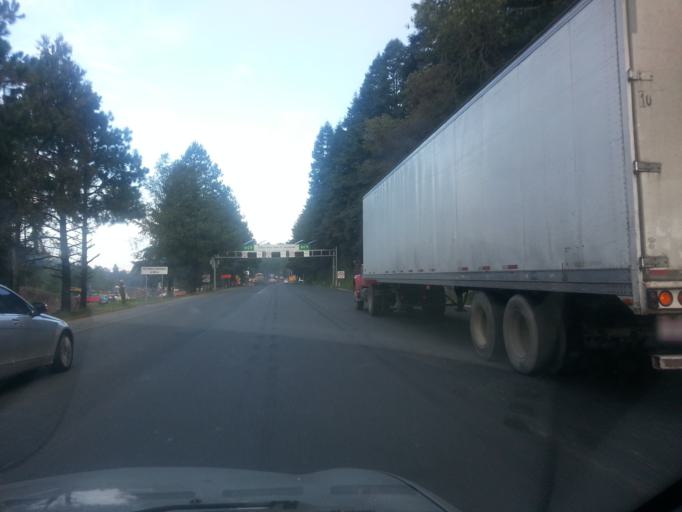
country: MX
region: Morelos
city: San Jeronimo Acazulco
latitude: 19.2989
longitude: -99.3978
